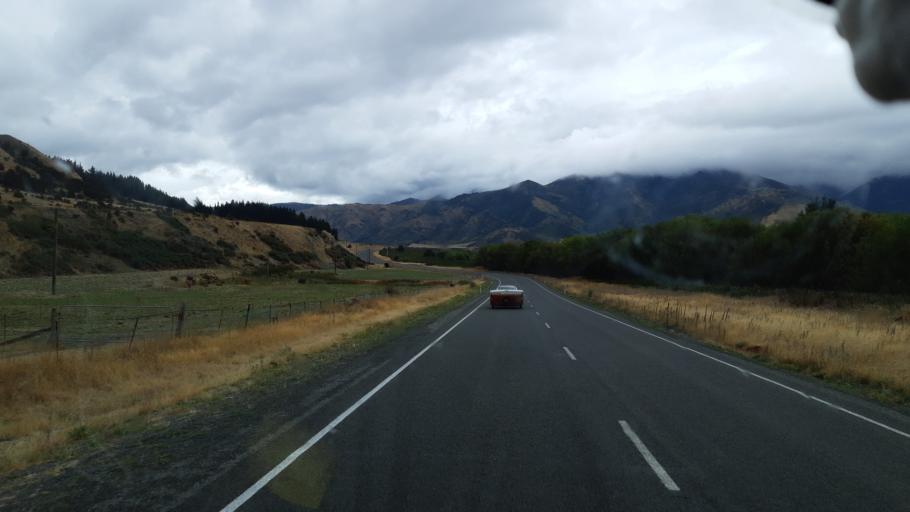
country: NZ
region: Canterbury
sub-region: Hurunui District
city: Amberley
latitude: -42.5741
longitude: 172.7196
